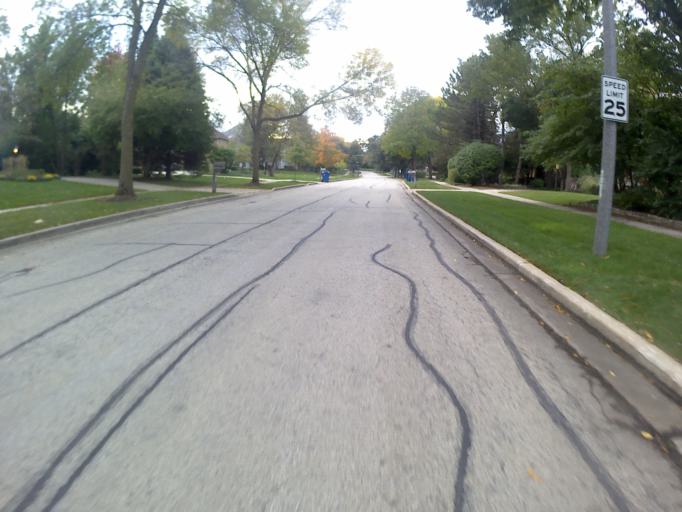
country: US
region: Illinois
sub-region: DuPage County
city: Lisle
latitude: 41.8133
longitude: -88.0983
